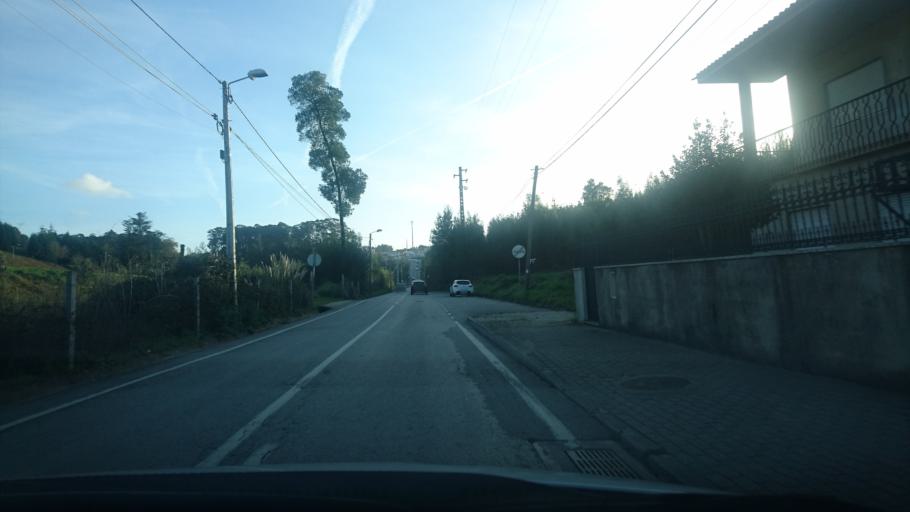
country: PT
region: Aveiro
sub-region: Espinho
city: Souto
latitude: 40.9782
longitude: -8.6044
